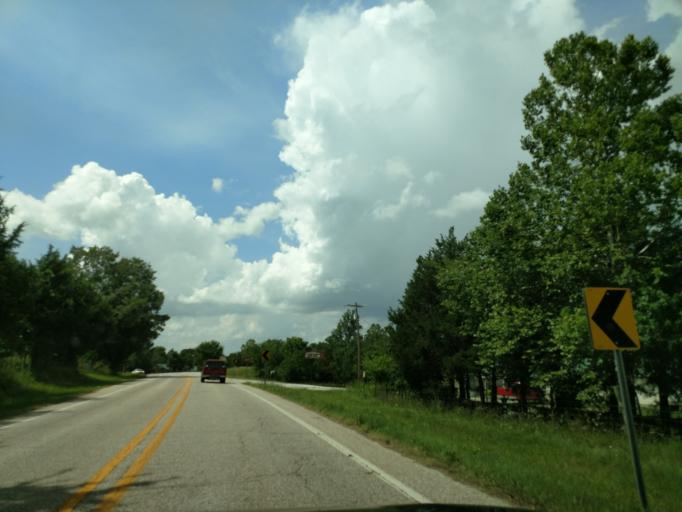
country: US
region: Arkansas
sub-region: Boone County
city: Harrison
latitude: 36.2878
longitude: -93.2358
